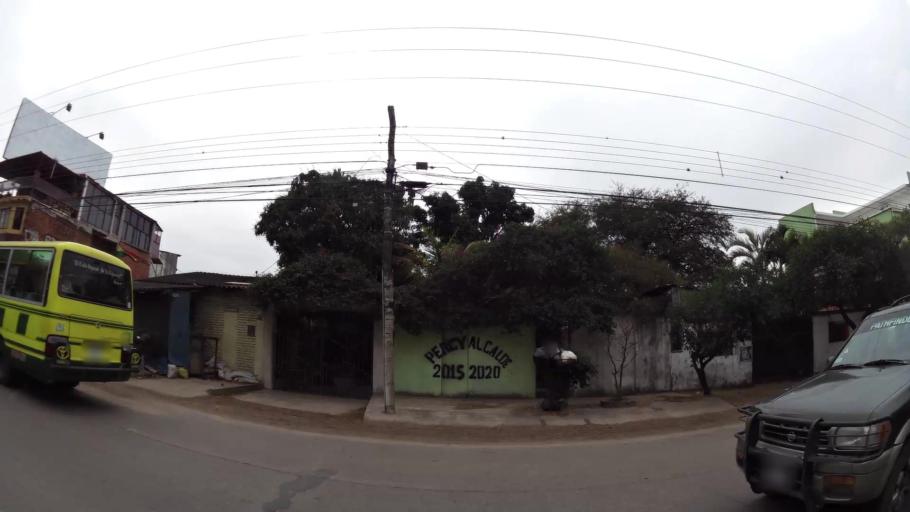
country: BO
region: Santa Cruz
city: Santa Cruz de la Sierra
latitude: -17.7526
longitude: -63.1942
